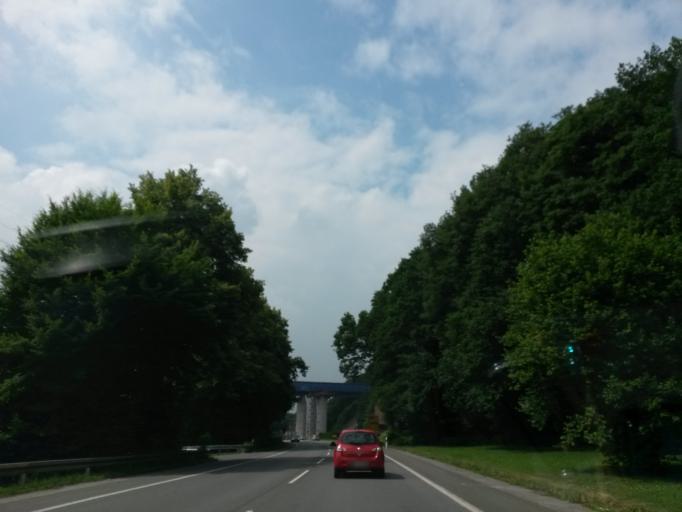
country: DE
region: North Rhine-Westphalia
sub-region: Regierungsbezirk Arnsberg
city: Hagen
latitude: 51.3858
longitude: 7.5287
